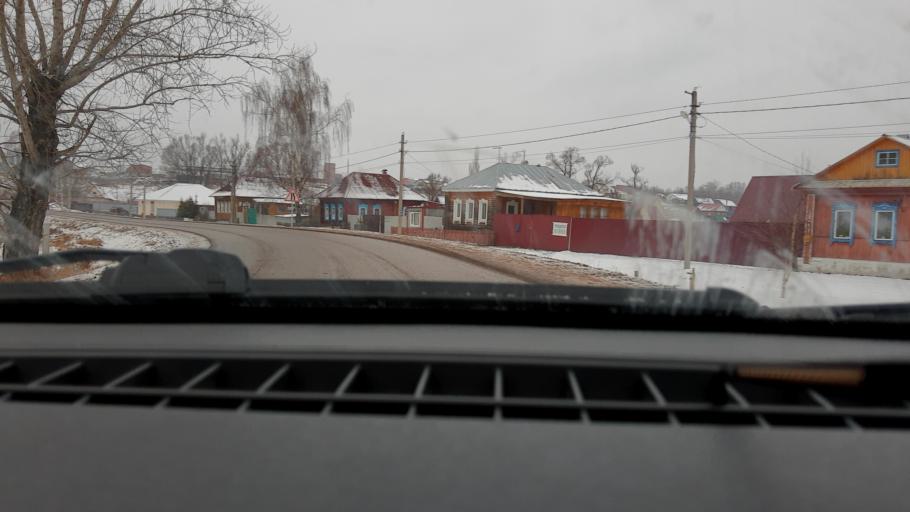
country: RU
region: Bashkortostan
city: Kabakovo
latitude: 54.7045
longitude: 56.2469
